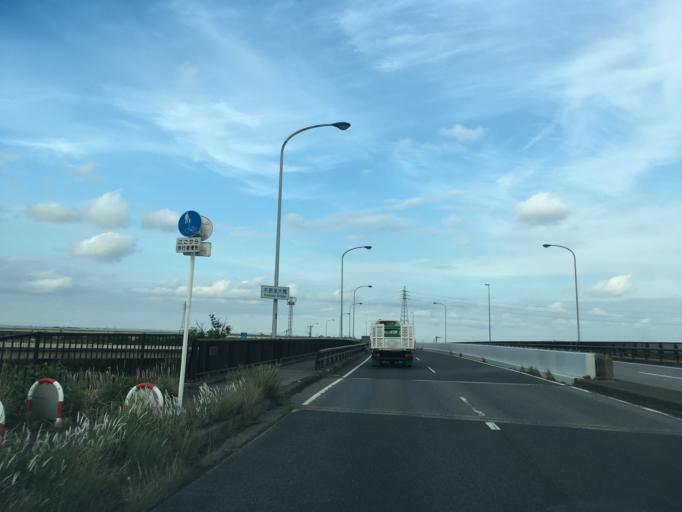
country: JP
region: Chiba
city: Kisarazu
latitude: 35.4093
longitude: 139.9508
